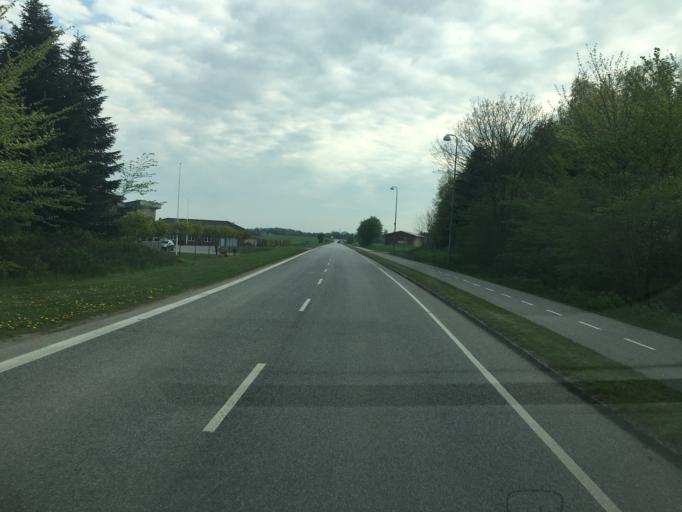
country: DK
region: South Denmark
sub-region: Haderslev Kommune
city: Haderslev
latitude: 55.2092
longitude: 9.4489
